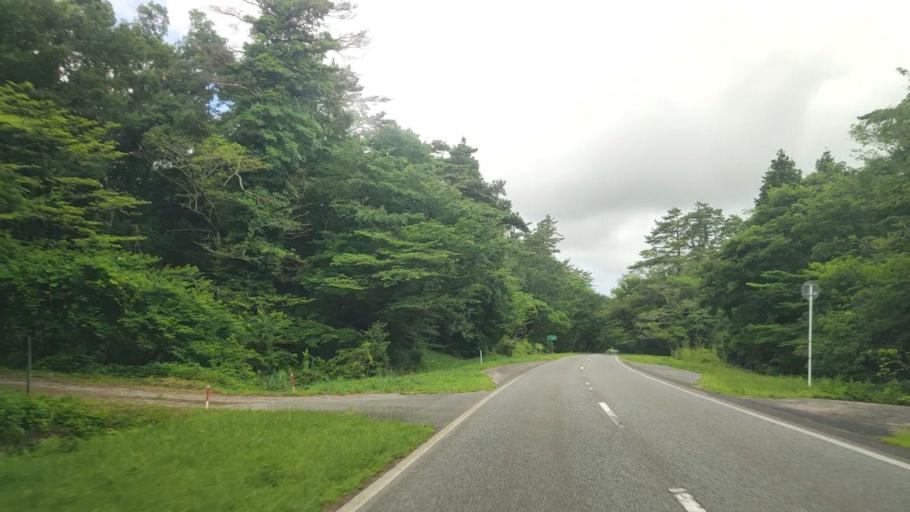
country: JP
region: Tottori
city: Yonago
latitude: 35.3996
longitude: 133.5004
